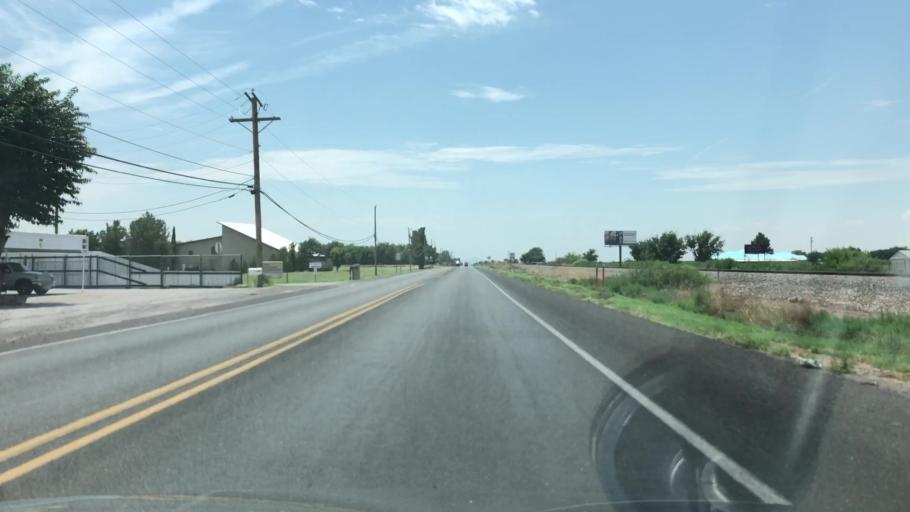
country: US
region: New Mexico
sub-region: Dona Ana County
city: University Park
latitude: 32.2545
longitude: -106.7534
